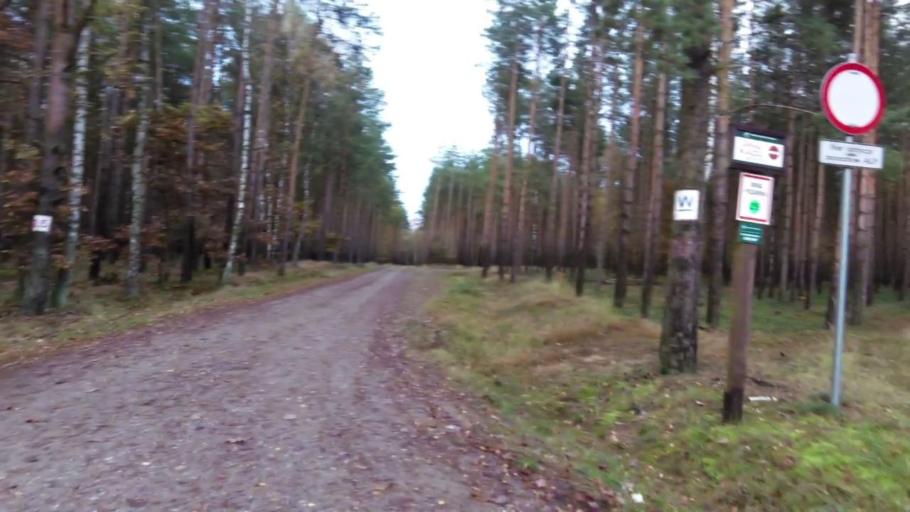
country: PL
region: West Pomeranian Voivodeship
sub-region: Powiat goleniowski
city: Stepnica
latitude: 53.6296
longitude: 14.7150
